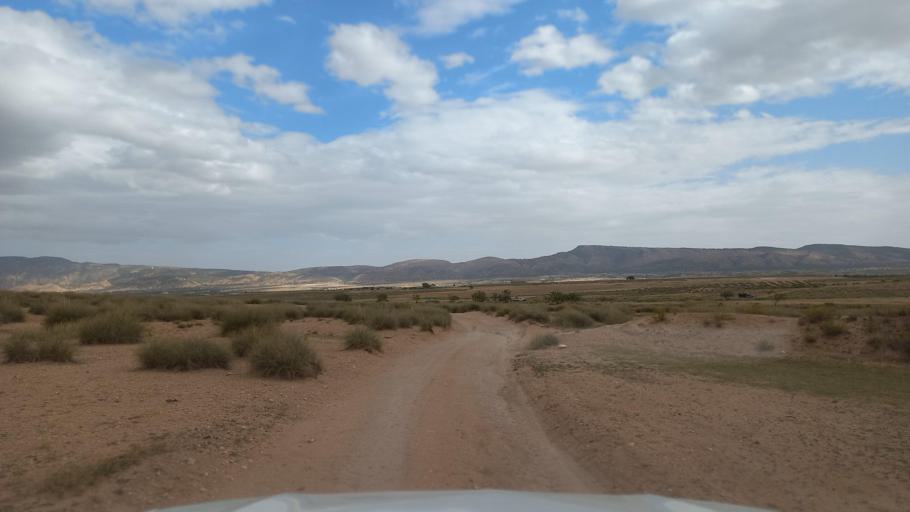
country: TN
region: Al Qasrayn
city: Sbiba
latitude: 35.3833
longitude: 9.1074
